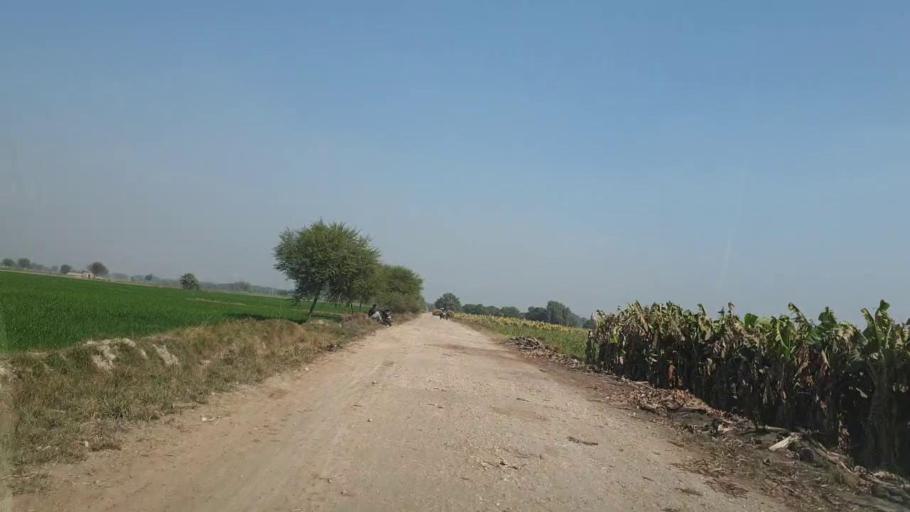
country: PK
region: Sindh
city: Matiari
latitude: 25.5384
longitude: 68.4735
